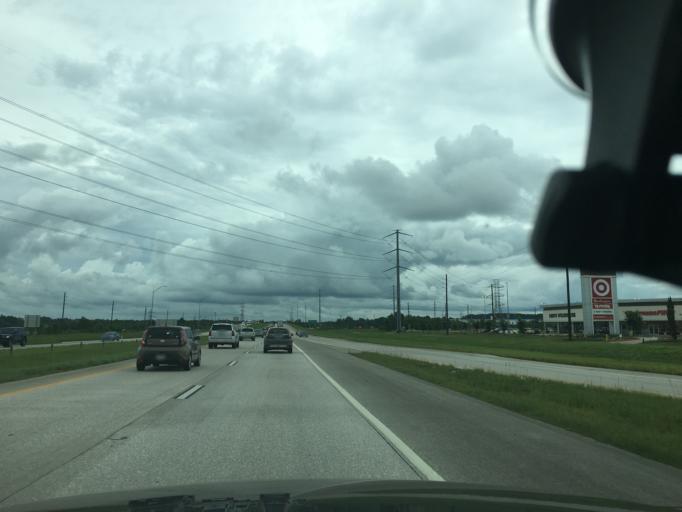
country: US
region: Texas
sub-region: Montgomery County
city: The Woodlands
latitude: 30.0891
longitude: -95.5223
